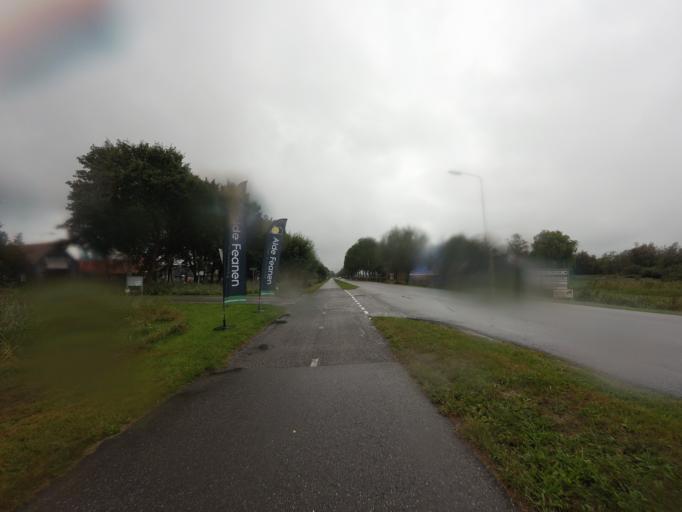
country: NL
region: Friesland
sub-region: Gemeente Tytsjerksteradiel
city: Garyp
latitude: 53.1371
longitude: 5.9492
